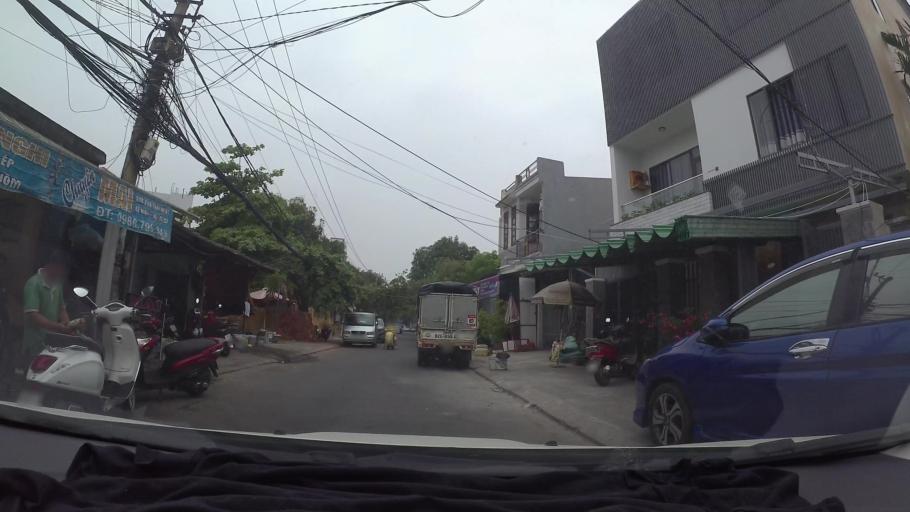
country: VN
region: Da Nang
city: Da Nang
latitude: 16.0457
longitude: 108.2084
